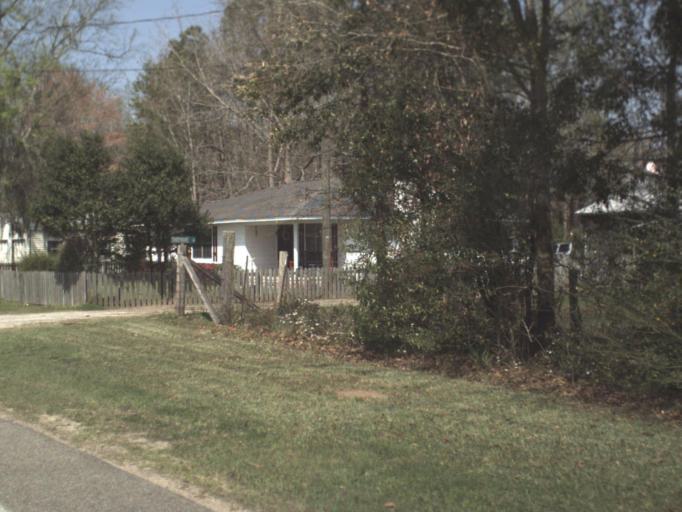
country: US
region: Florida
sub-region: Liberty County
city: Bristol
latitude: 30.4319
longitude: -84.9675
